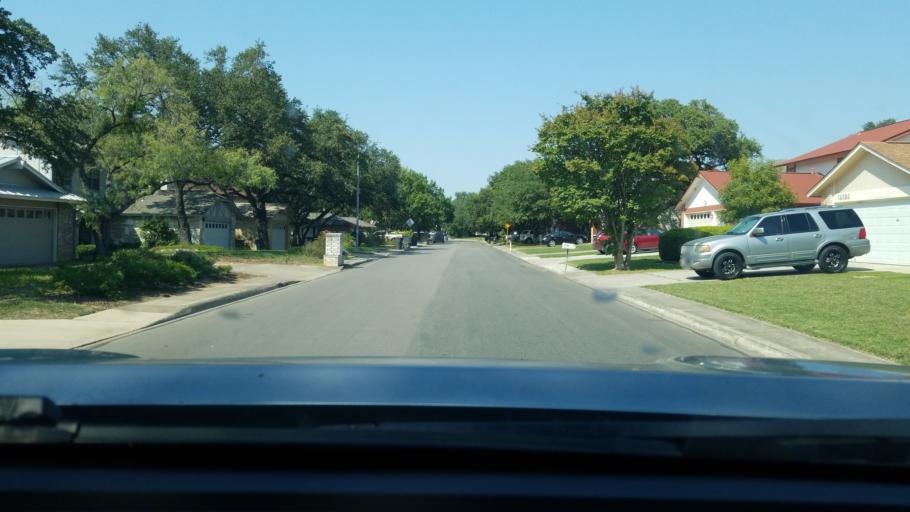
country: US
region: Texas
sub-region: Bexar County
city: Shavano Park
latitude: 29.5603
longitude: -98.6059
